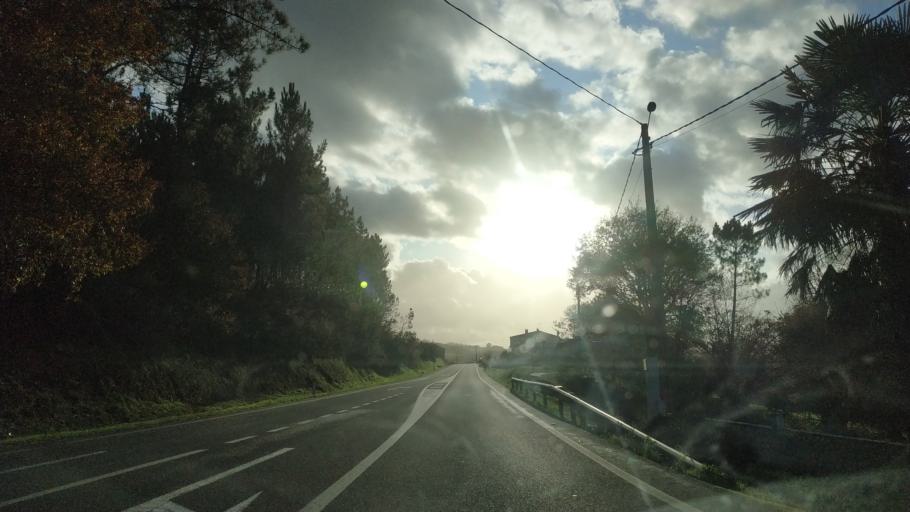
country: ES
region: Galicia
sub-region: Provincia de Pontevedra
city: Silleda
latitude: 42.7861
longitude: -8.1683
